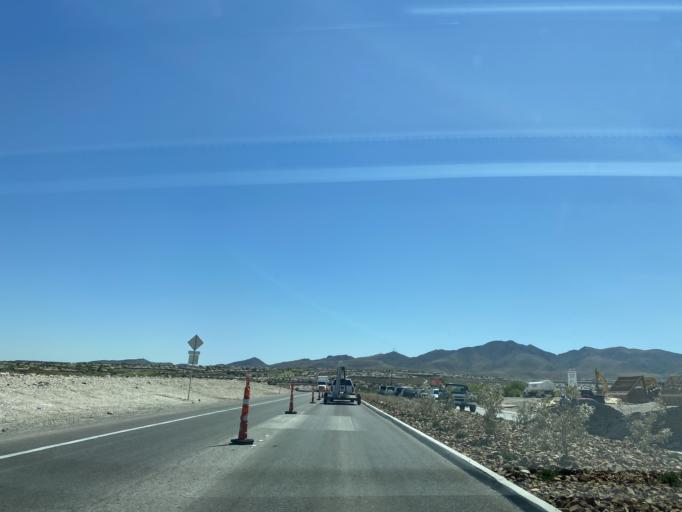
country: US
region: Nevada
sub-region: Clark County
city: Whitney
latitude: 35.9400
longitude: -115.1311
